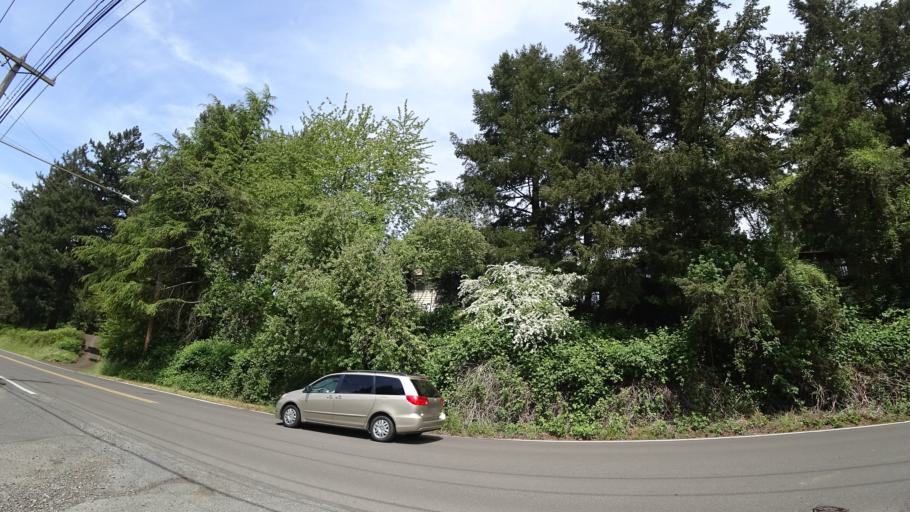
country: US
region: Oregon
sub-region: Clackamas County
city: Milwaukie
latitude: 45.4622
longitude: -122.6040
